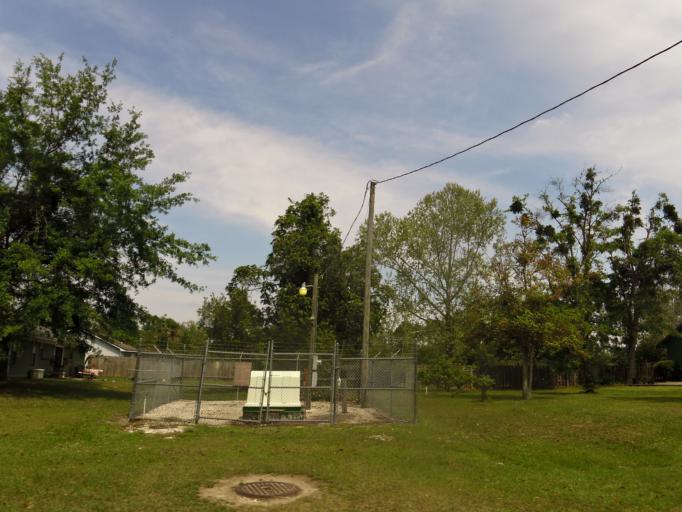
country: US
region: Georgia
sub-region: Camden County
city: Kingsland
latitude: 30.7658
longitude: -81.6600
